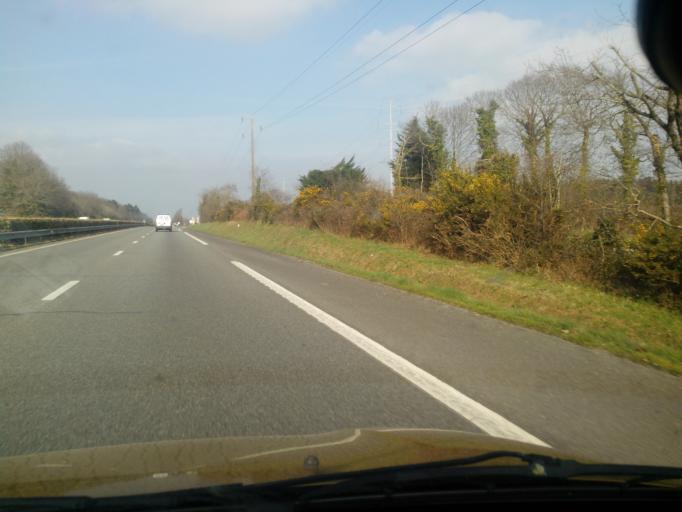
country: FR
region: Brittany
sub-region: Departement du Morbihan
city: Saint-Nolff
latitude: 47.6819
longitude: -2.6501
